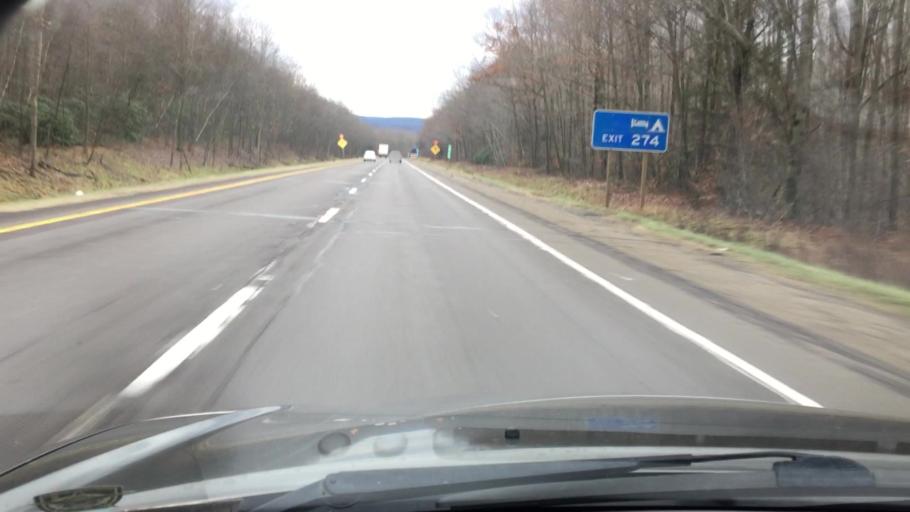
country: US
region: Pennsylvania
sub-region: Luzerne County
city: White Haven
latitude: 41.0600
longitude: -75.7160
